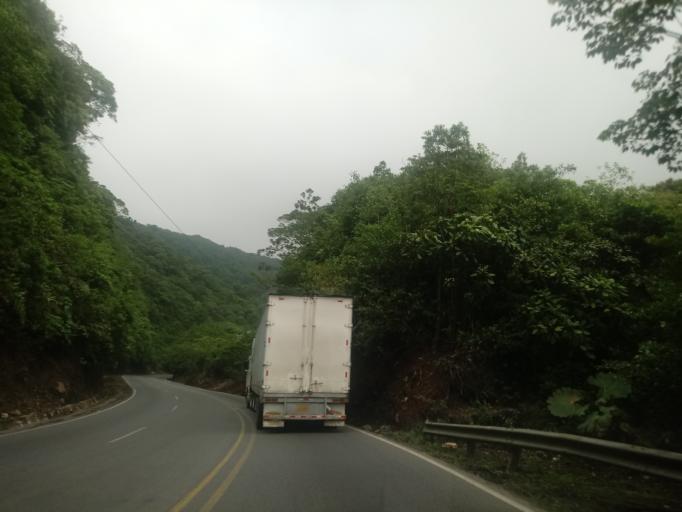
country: CR
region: Heredia
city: Angeles
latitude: 10.0562
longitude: -84.0083
